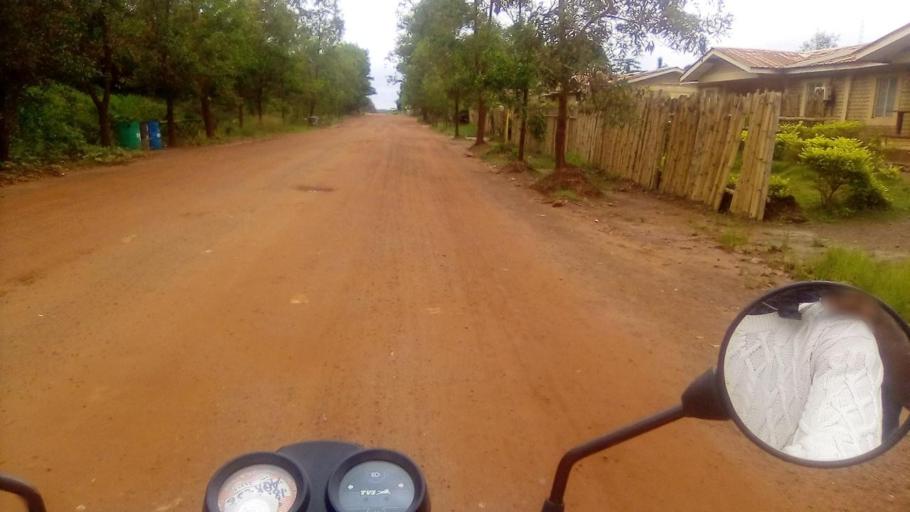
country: SL
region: Southern Province
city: Tongole
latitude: 7.4351
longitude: -11.8447
